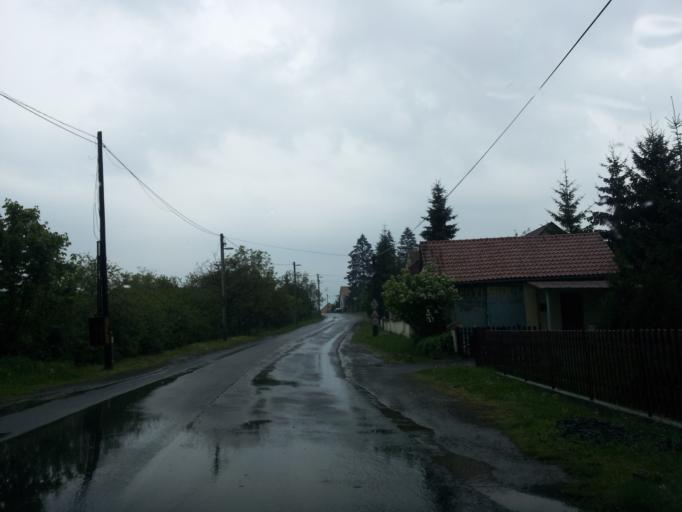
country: HU
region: Baranya
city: Hosszuheteny
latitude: 46.1823
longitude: 18.3194
